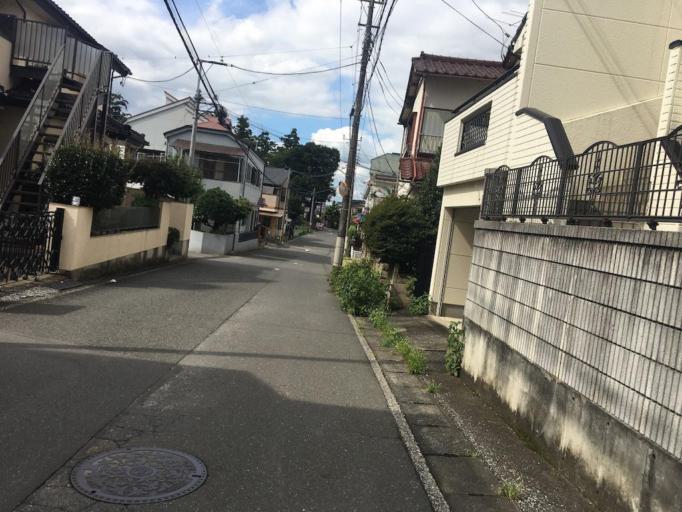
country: JP
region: Saitama
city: Kawagoe
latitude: 35.8918
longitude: 139.5022
